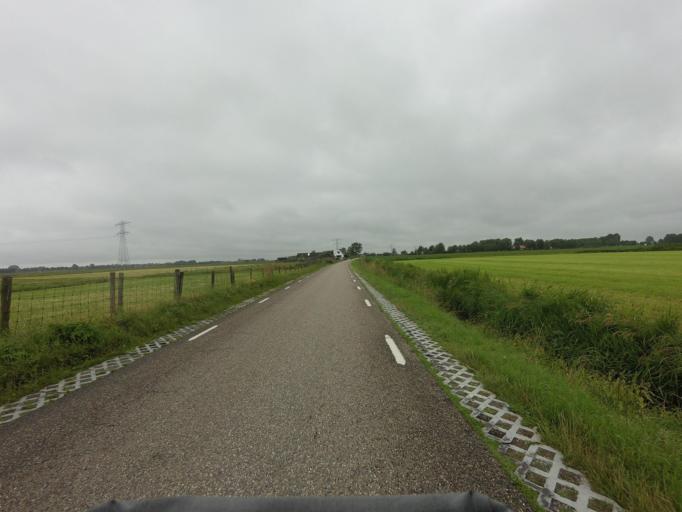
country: NL
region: North Holland
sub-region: Gemeente Schagen
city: Schagen
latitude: 52.7794
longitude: 4.8281
